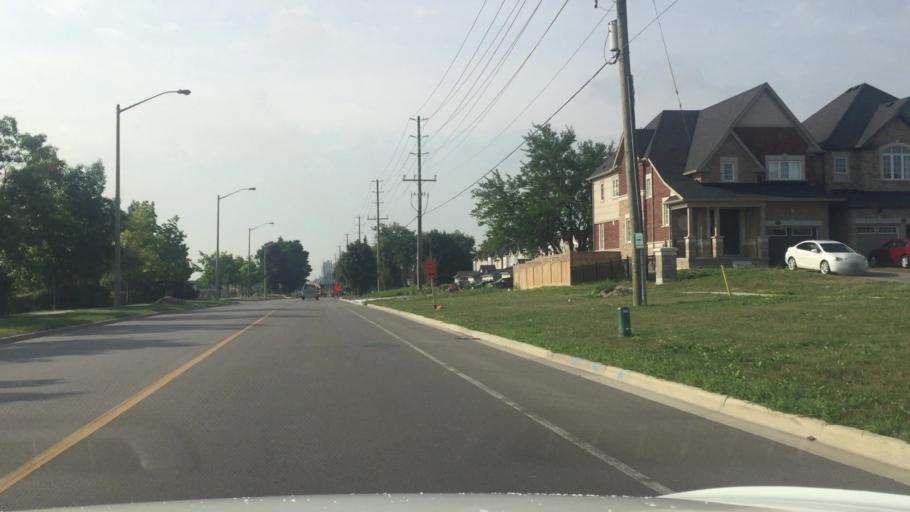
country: CA
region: Ontario
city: Oshawa
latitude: 43.9083
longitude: -78.7116
